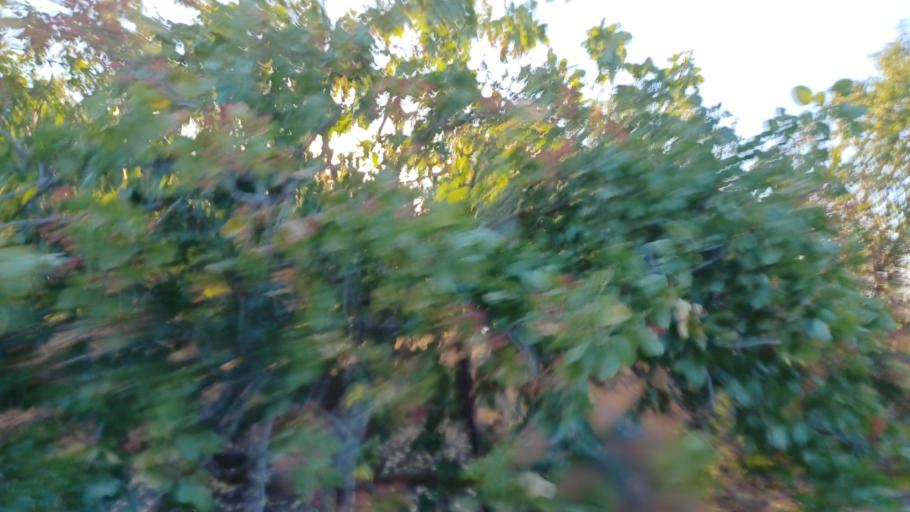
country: CY
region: Pafos
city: Mesogi
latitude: 34.8600
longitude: 32.6202
